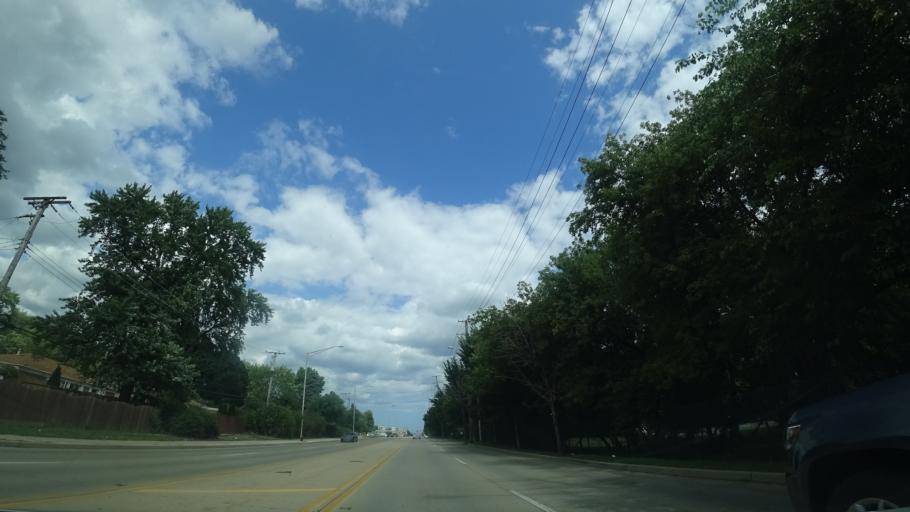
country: US
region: Illinois
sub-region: Cook County
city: Merrionette Park
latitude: 41.6912
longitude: -87.7244
